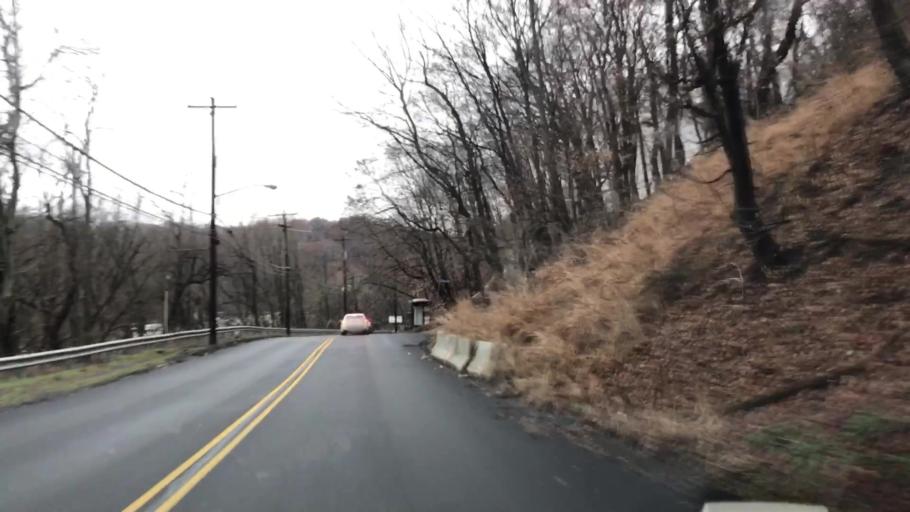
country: US
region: Pennsylvania
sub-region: Allegheny County
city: Green Tree
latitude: 40.4313
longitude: -80.0390
